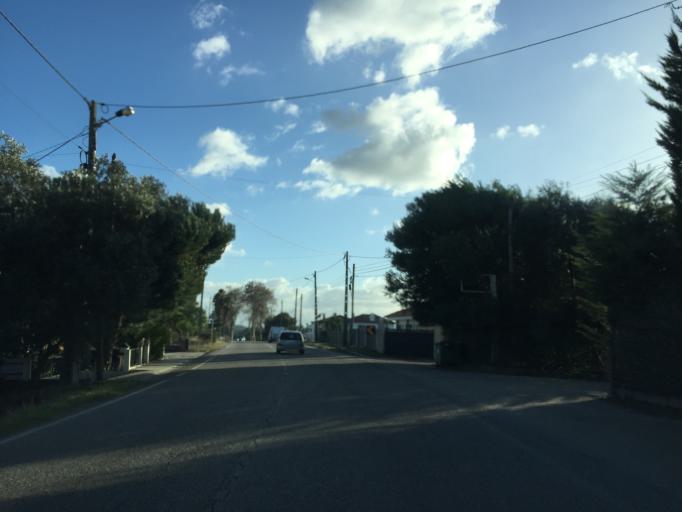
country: PT
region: Leiria
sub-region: Leiria
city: Monte Redondo
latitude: 39.8873
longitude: -8.8373
